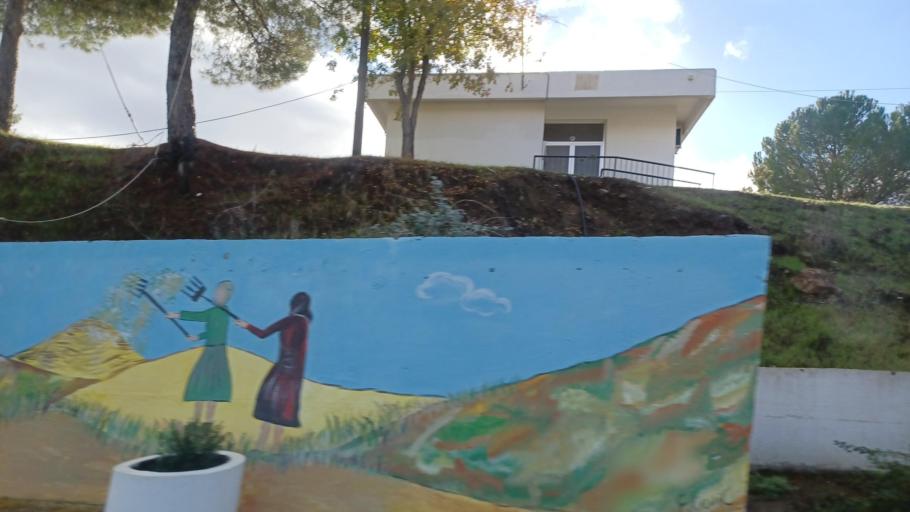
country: CY
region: Lefkosia
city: Lythrodontas
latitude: 34.9611
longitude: 33.3334
